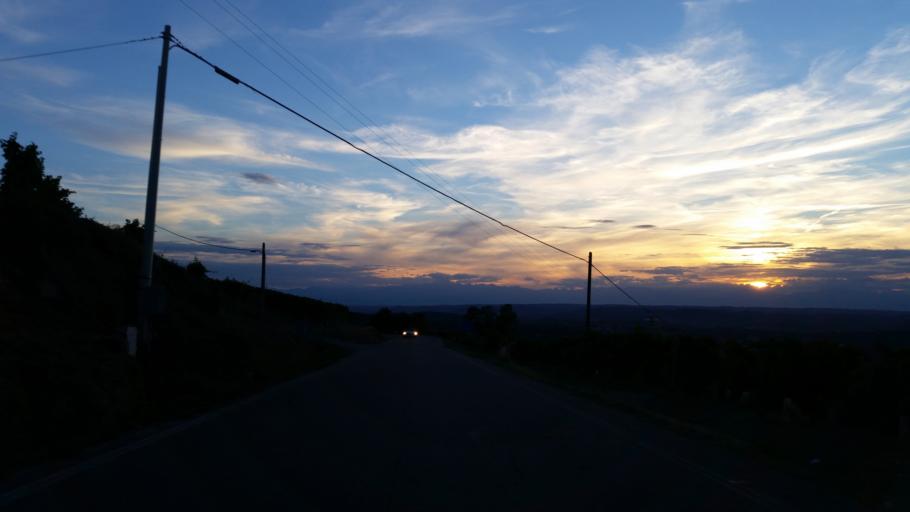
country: IT
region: Piedmont
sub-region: Provincia di Cuneo
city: Castiglione Tinella
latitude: 44.7184
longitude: 8.1858
